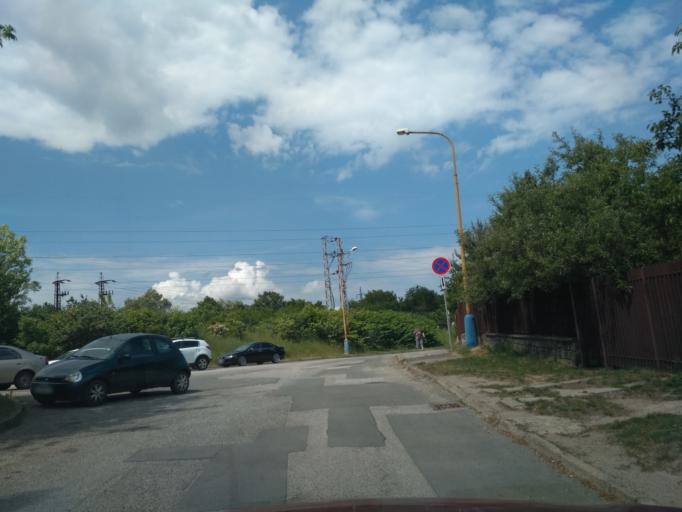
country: SK
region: Kosicky
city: Kosice
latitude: 48.7293
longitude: 21.2314
